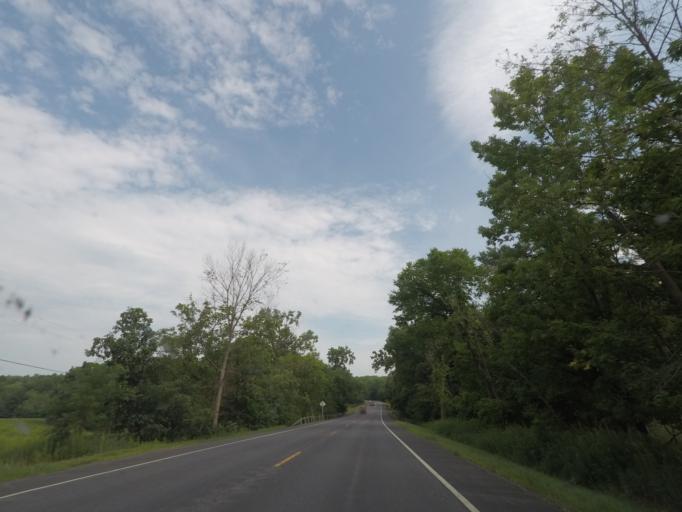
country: US
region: New York
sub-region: Rensselaer County
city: Poestenkill
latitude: 42.7245
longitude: -73.5558
